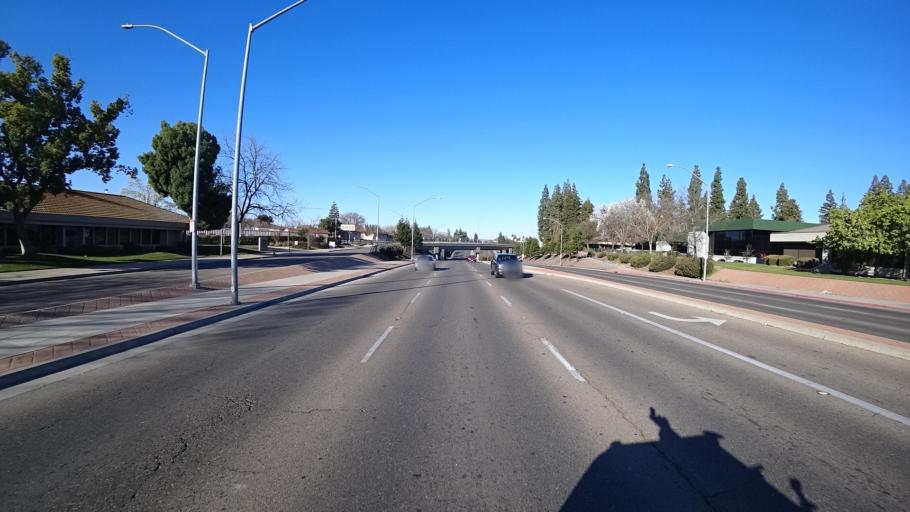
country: US
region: California
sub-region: Fresno County
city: Fresno
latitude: 36.8082
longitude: -119.8390
